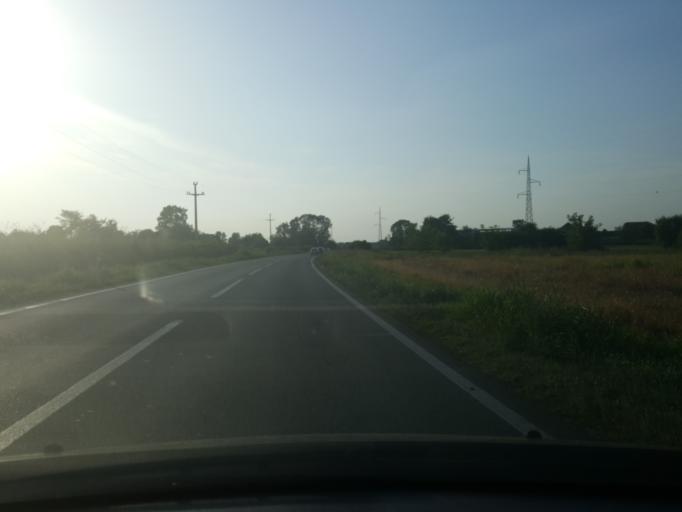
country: RS
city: Majur
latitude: 44.7661
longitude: 19.6324
